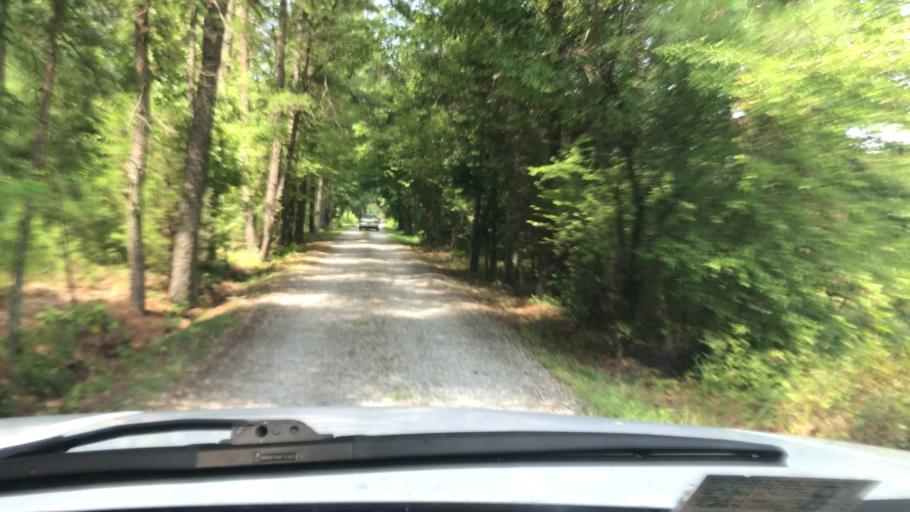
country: US
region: Virginia
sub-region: Henrico County
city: Short Pump
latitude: 37.6491
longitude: -77.6792
